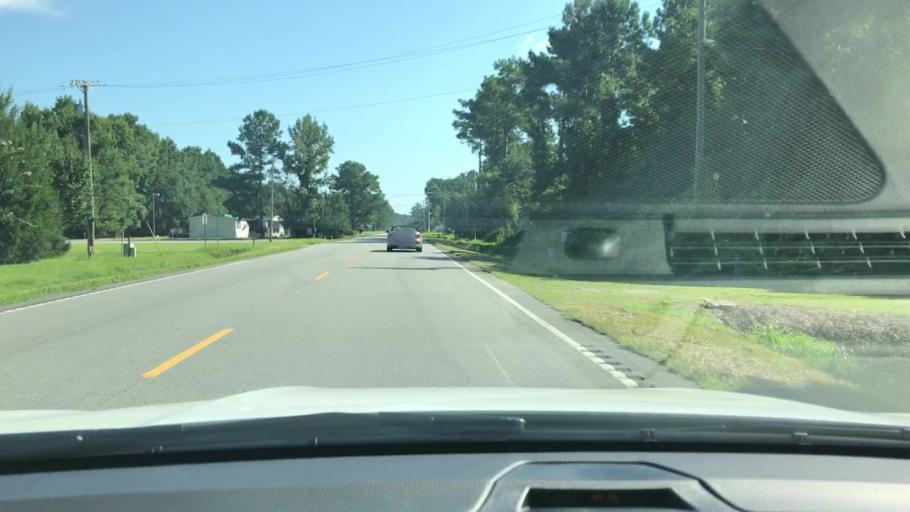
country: US
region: South Carolina
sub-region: Horry County
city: Socastee
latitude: 33.6887
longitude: -79.1197
